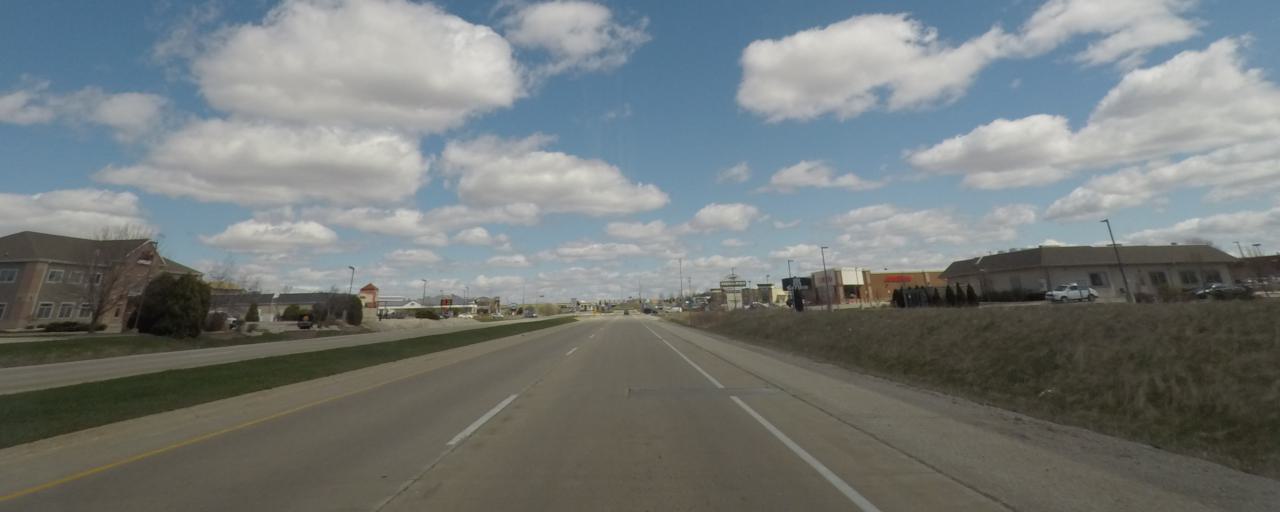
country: US
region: Wisconsin
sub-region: Jefferson County
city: Johnson Creek
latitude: 43.0807
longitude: -88.7644
